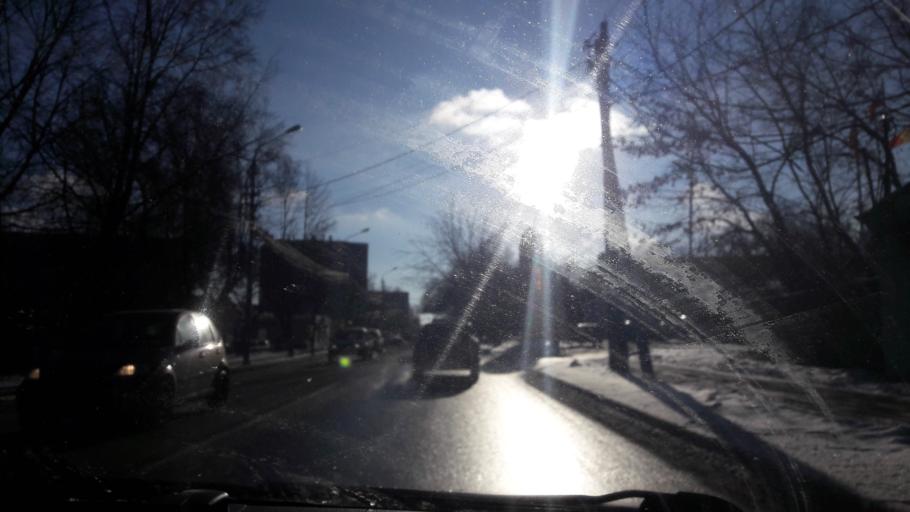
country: RU
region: Tula
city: Tula
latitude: 54.1766
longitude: 37.6228
